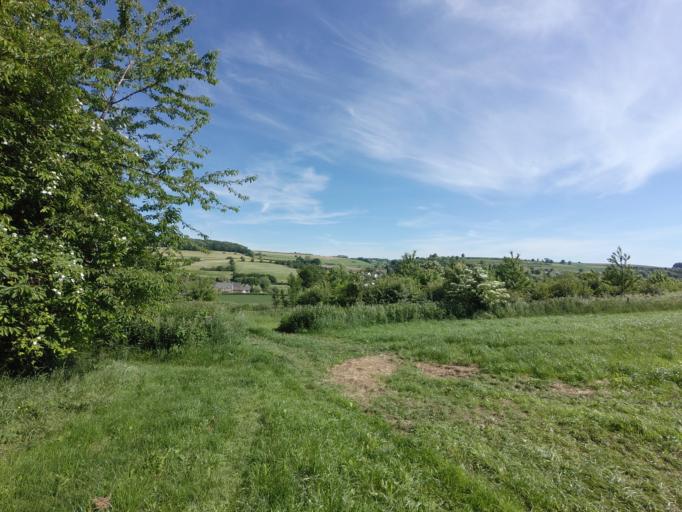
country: NL
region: Limburg
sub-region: Gemeente Voerendaal
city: Ubachsberg
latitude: 50.8217
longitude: 5.9297
